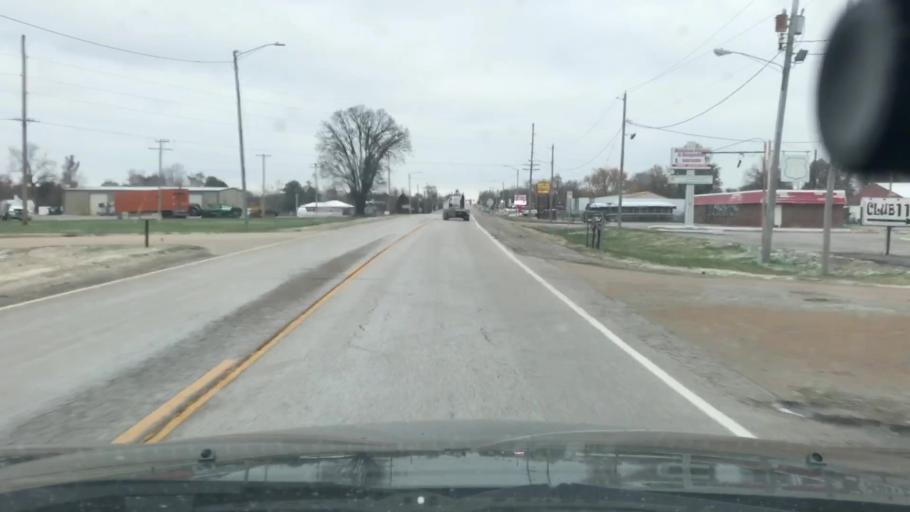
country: US
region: Illinois
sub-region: Madison County
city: Pontoon Beach
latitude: 38.7173
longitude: -90.0707
